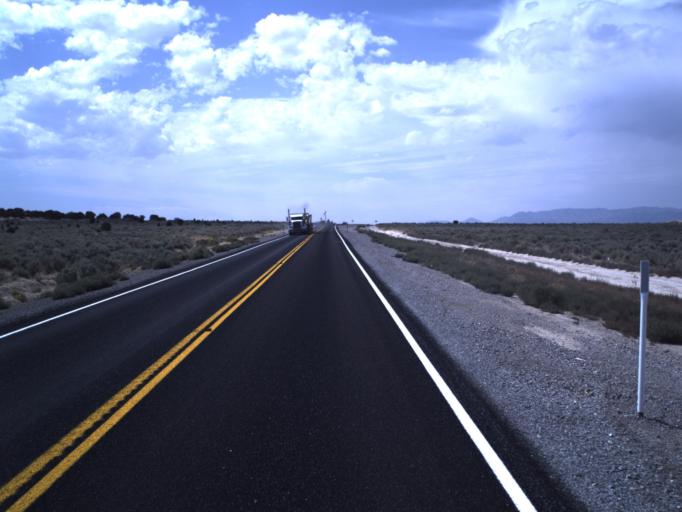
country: US
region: Utah
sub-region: Utah County
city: Eagle Mountain
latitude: 40.2333
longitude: -112.1723
